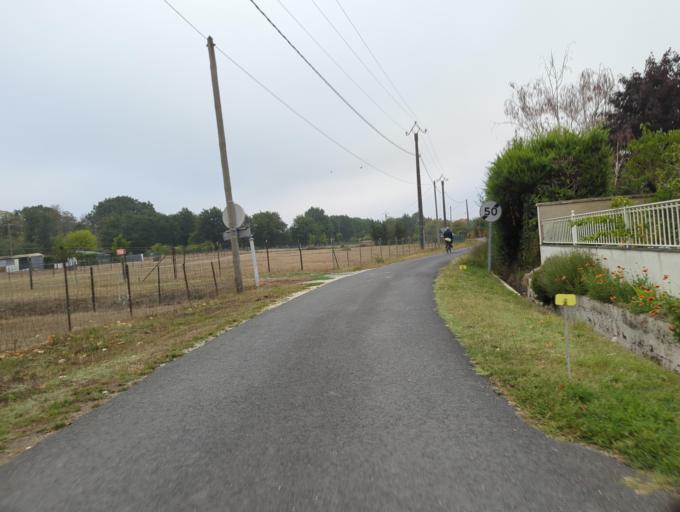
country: FR
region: Pays de la Loire
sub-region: Departement de Maine-et-Loire
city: Le Plessis-Grammoire
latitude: 47.4740
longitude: -0.4395
